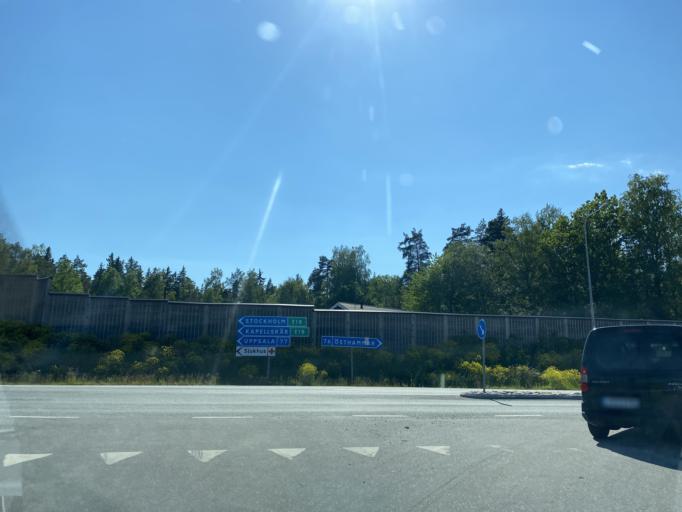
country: SE
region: Stockholm
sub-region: Norrtalje Kommun
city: Norrtalje
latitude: 59.7709
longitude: 18.6796
